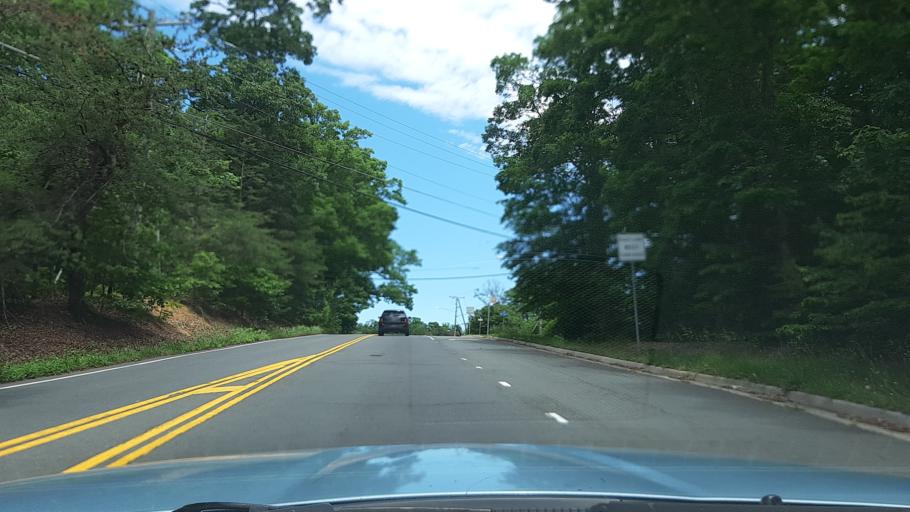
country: US
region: Virginia
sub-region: Fairfax County
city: Newington
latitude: 38.7286
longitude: -77.2095
